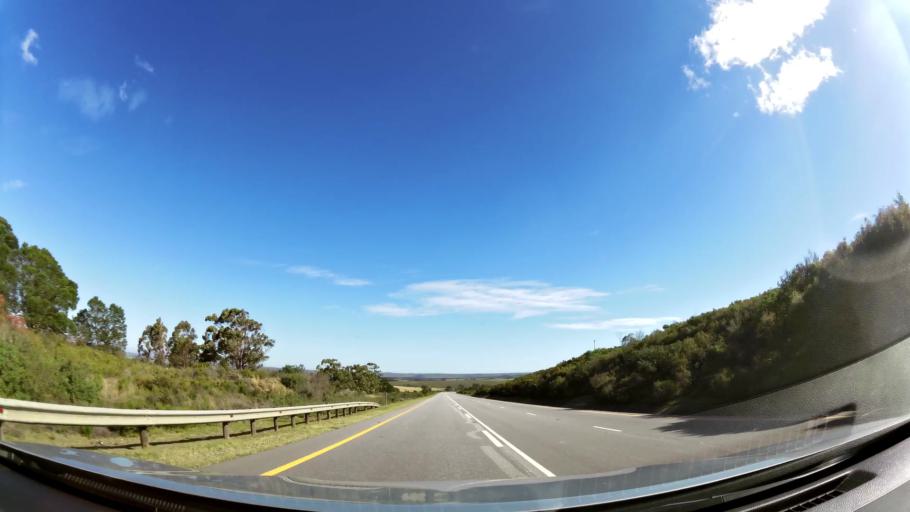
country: ZA
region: Eastern Cape
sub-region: Cacadu District Municipality
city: Kruisfontein
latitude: -34.0019
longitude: 24.6813
